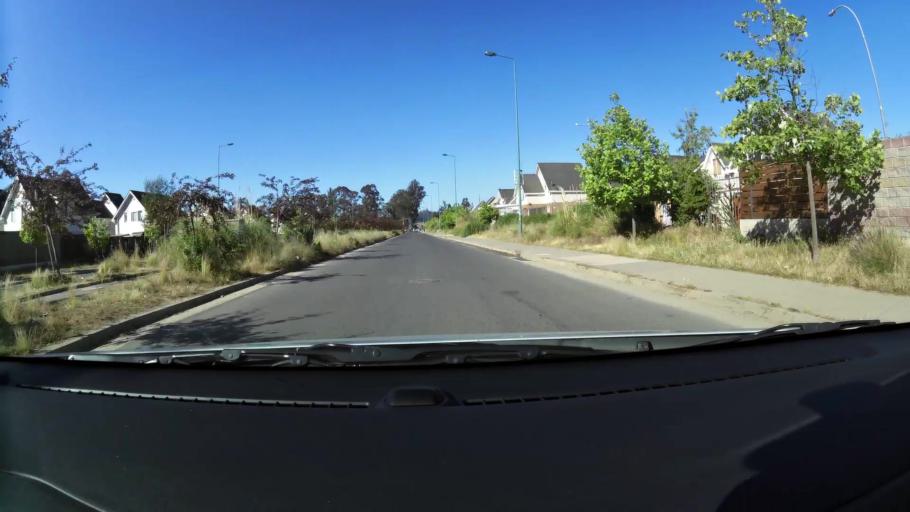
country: CL
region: Valparaiso
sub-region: Provincia de Valparaiso
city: Valparaiso
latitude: -33.1221
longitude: -71.5757
